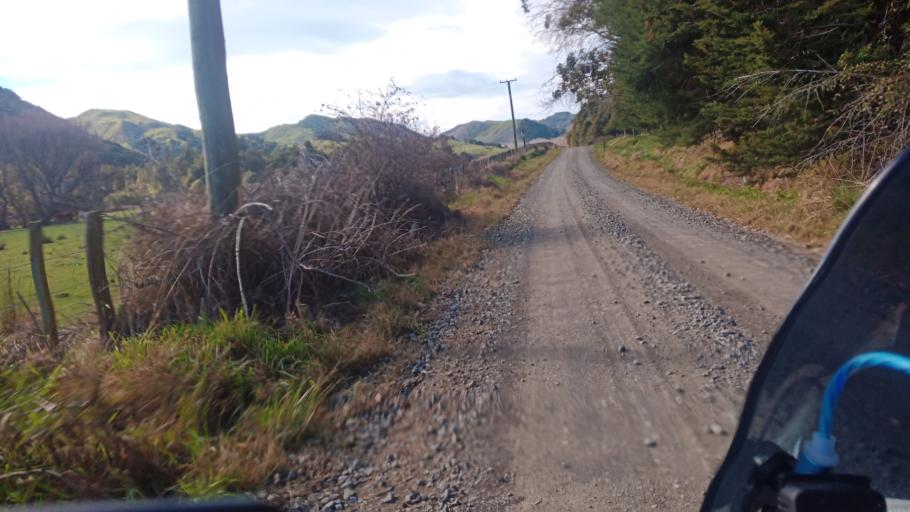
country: NZ
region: Gisborne
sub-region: Gisborne District
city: Gisborne
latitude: -38.2935
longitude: 178.2796
